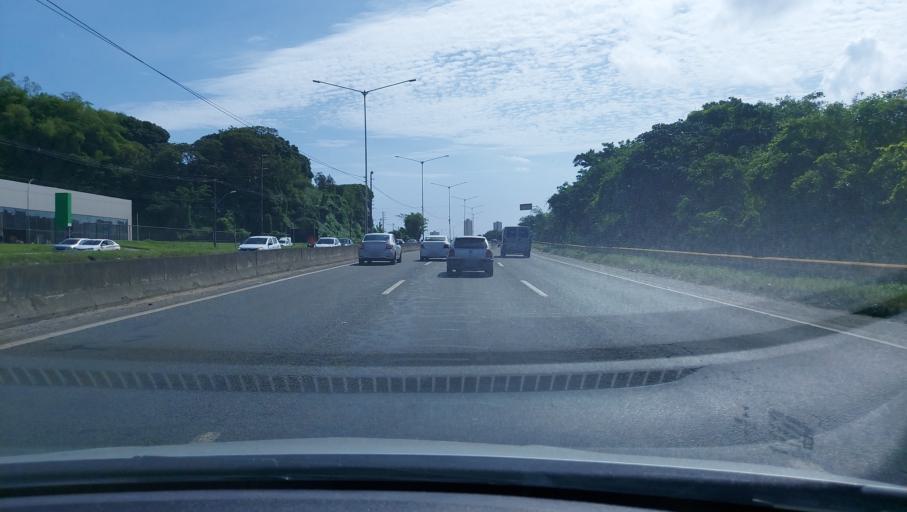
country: BR
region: Bahia
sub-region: Salvador
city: Salvador
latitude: -12.9598
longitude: -38.4737
